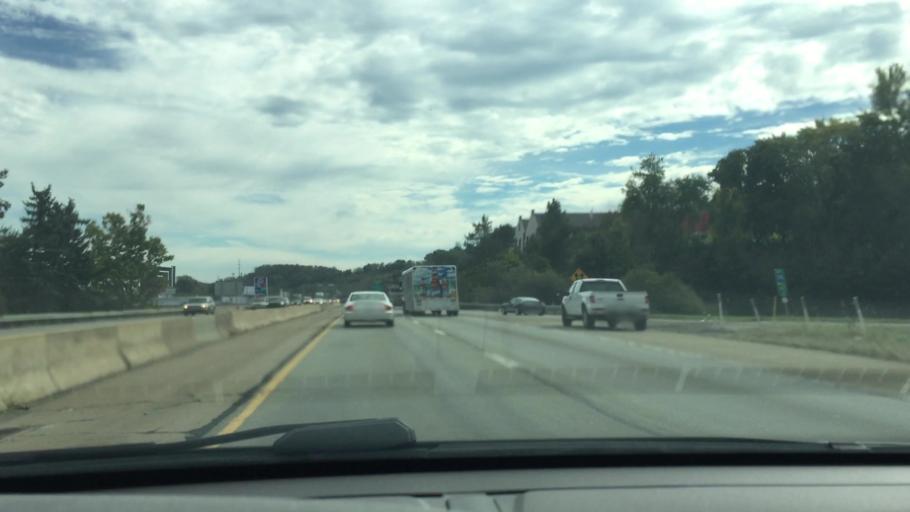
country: US
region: Pennsylvania
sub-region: Allegheny County
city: Rennerdale
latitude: 40.4307
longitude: -80.1363
